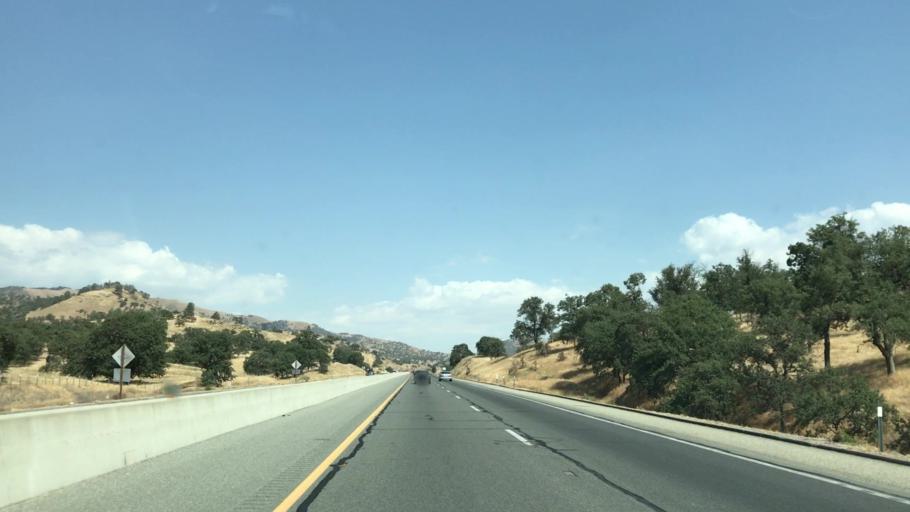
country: US
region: California
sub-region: Kern County
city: Golden Hills
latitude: 35.2129
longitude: -118.5472
